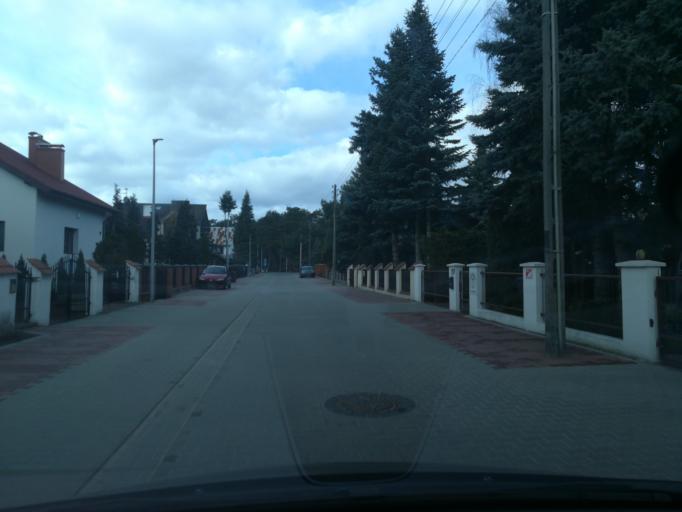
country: PL
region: Kujawsko-Pomorskie
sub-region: Powiat torunski
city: Lubicz Dolny
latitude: 52.9750
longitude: 18.6791
